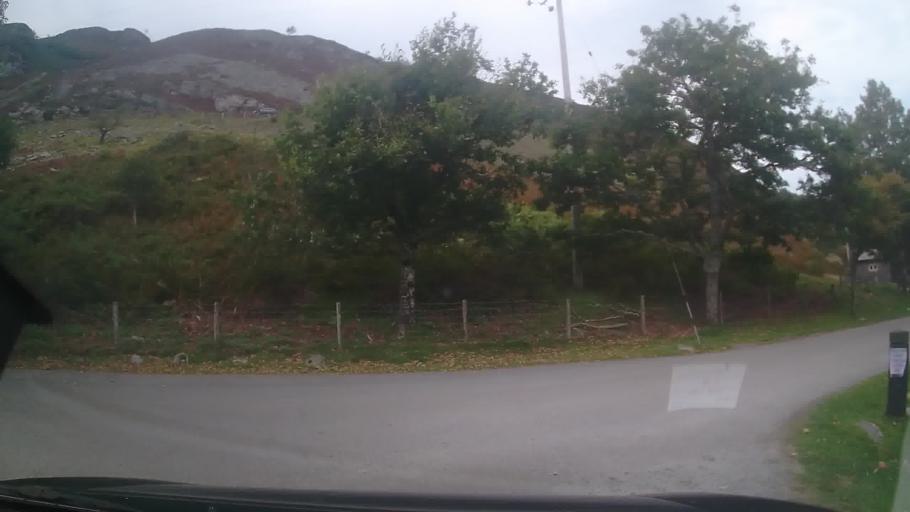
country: GB
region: Wales
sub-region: Sir Powys
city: Rhayader
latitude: 52.2702
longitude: -3.5704
